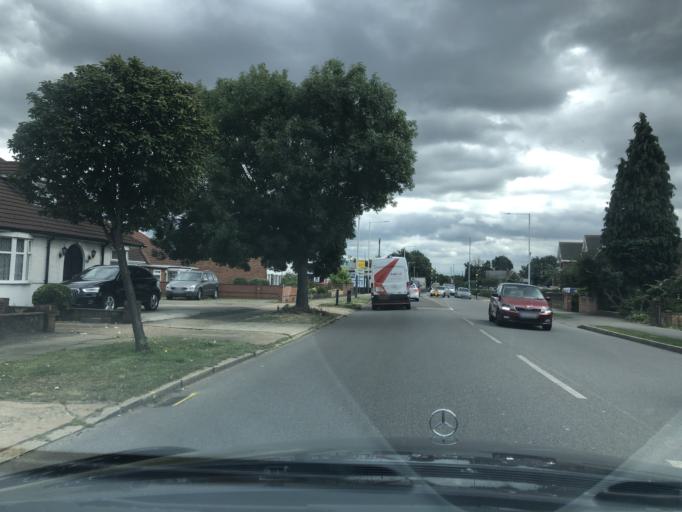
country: GB
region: England
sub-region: Greater London
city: Ruislip
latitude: 51.5509
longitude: -0.4013
